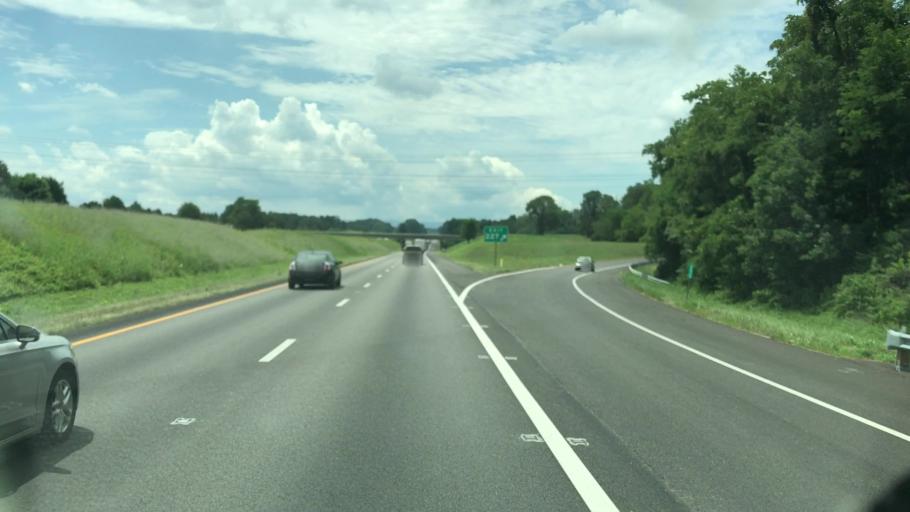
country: US
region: Virginia
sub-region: Augusta County
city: Verona
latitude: 38.1968
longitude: -78.9960
